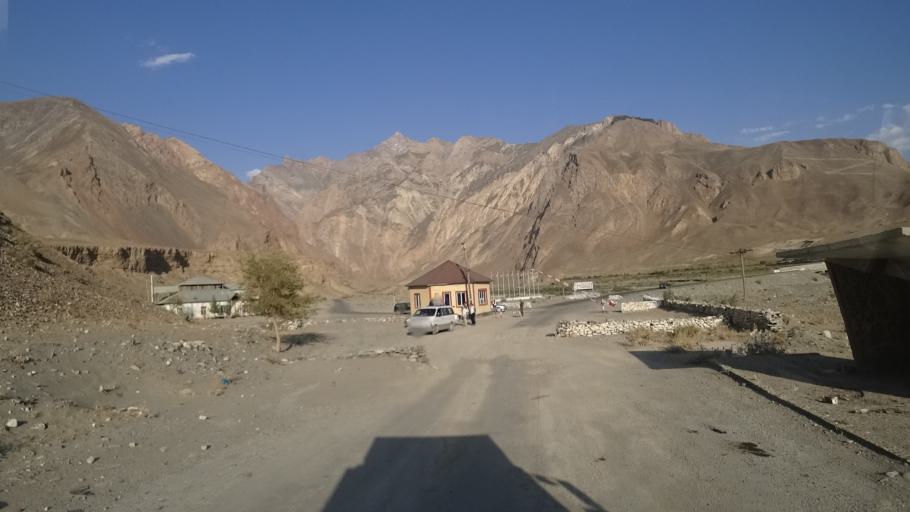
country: TJ
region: Gorno-Badakhshan
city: Vanj
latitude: 38.3001
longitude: 71.3361
